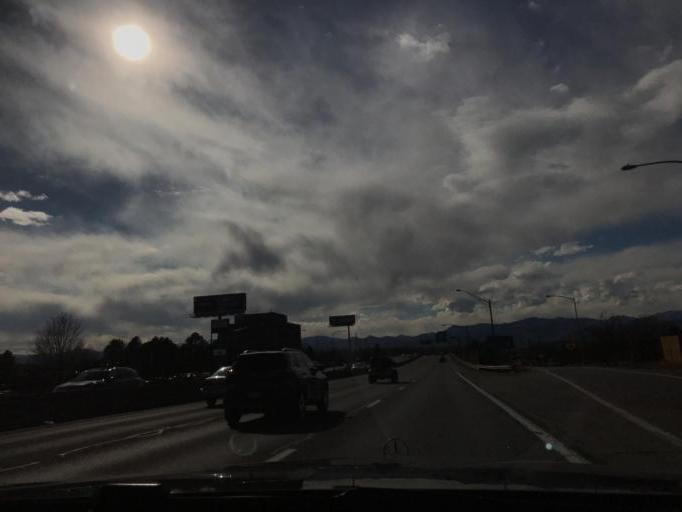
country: US
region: Colorado
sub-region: Jefferson County
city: Wheat Ridge
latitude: 39.7836
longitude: -105.0576
